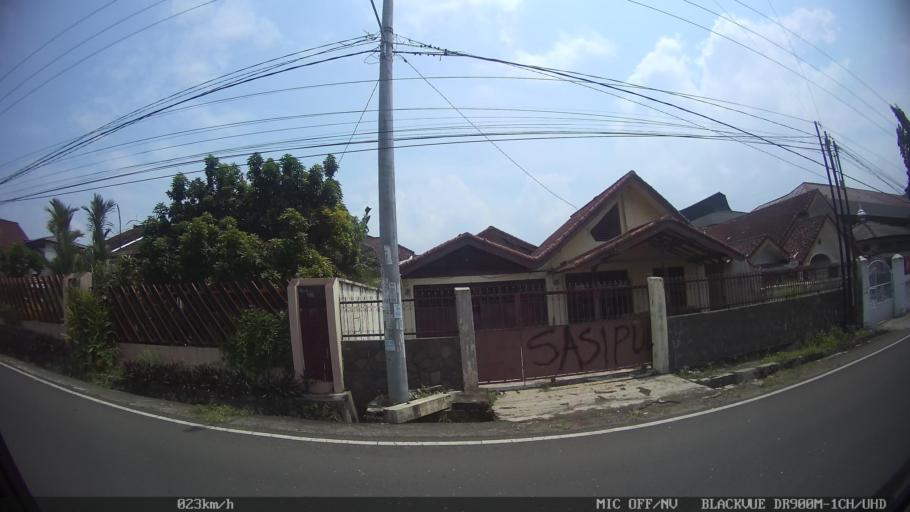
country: ID
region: Lampung
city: Bandarlampung
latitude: -5.4310
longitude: 105.2747
